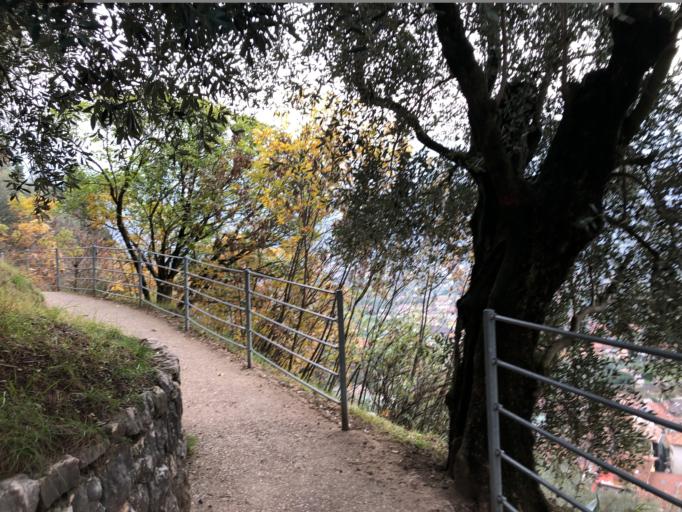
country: IT
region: Trentino-Alto Adige
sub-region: Provincia di Trento
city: Arco
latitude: 45.9205
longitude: 10.8864
